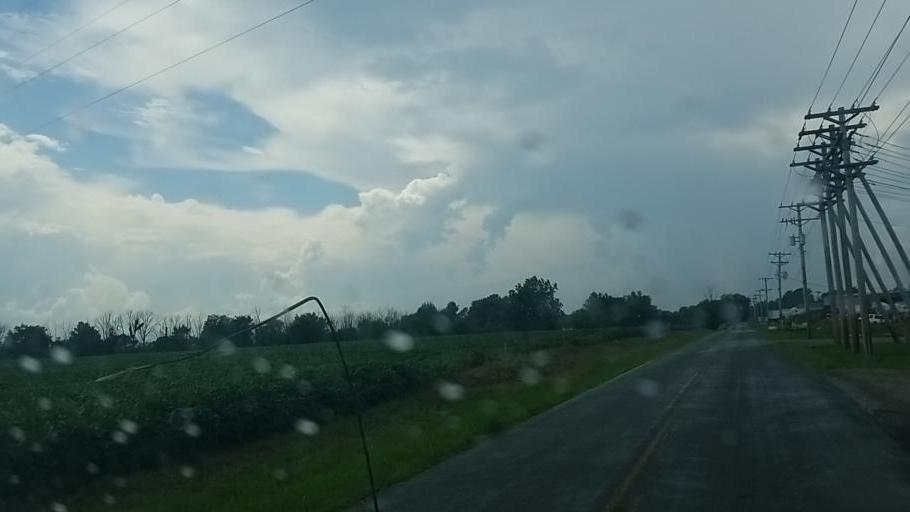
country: US
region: Ohio
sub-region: Lorain County
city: Grafton
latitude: 41.1582
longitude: -82.0178
